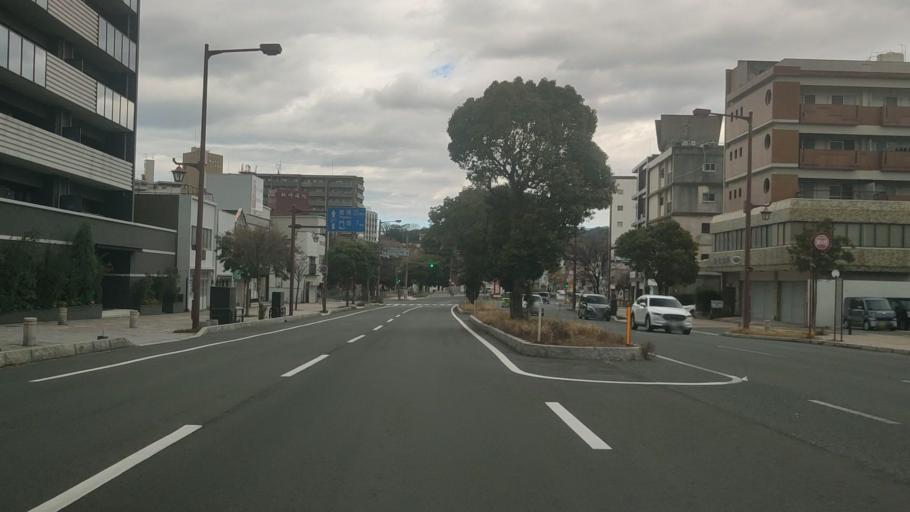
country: JP
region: Yamaguchi
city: Shimonoseki
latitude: 33.9594
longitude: 130.9420
